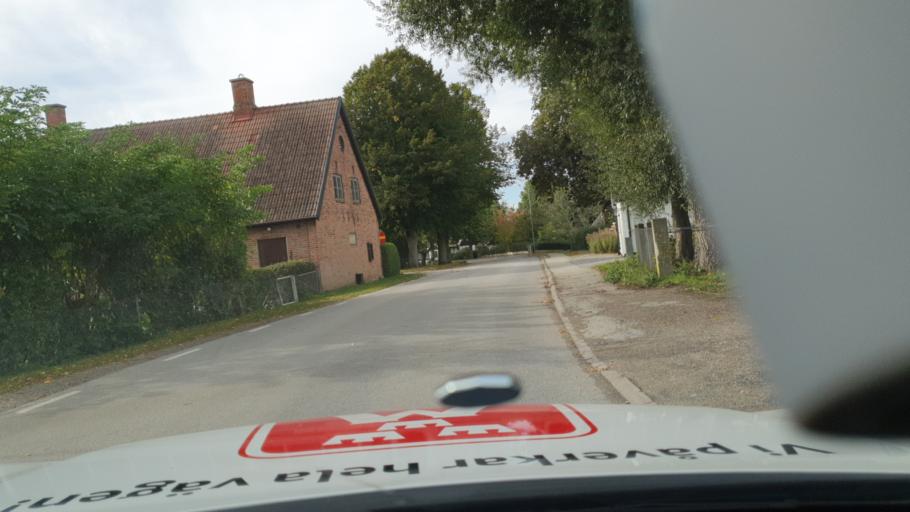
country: SE
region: Skane
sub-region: Malmo
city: Oxie
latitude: 55.5158
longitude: 13.0853
